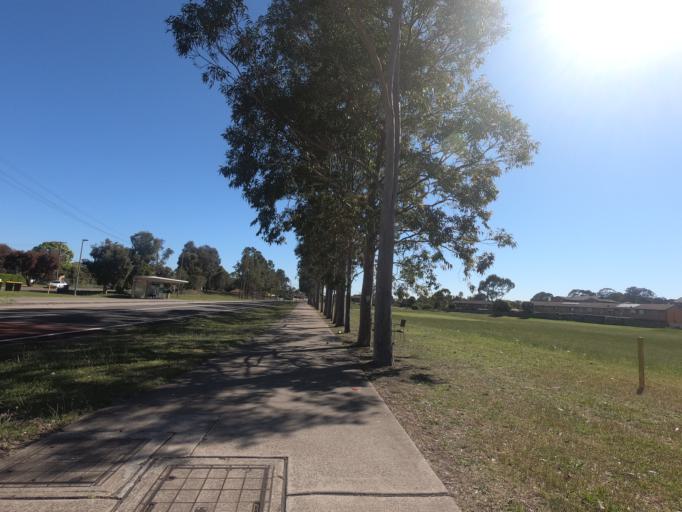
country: AU
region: New South Wales
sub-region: Fairfield
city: Cabramatta West
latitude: -33.9234
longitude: 150.9132
